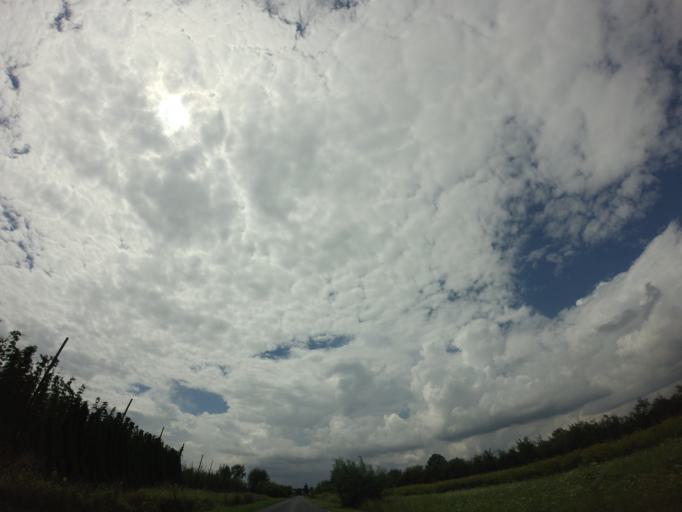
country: PL
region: Lublin Voivodeship
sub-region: Powiat opolski
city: Wilkow
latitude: 51.2638
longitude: 21.8834
